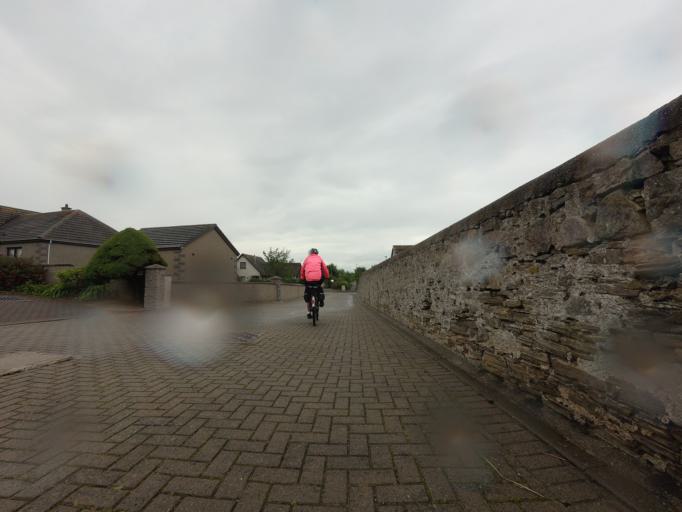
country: GB
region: Scotland
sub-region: Moray
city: Buckie
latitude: 57.6827
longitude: -2.9398
